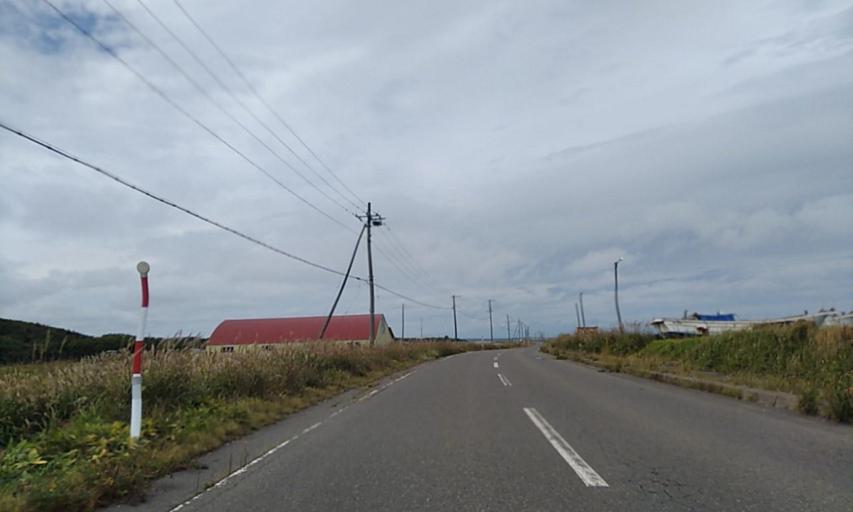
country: JP
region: Hokkaido
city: Shibetsu
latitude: 43.6079
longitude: 145.2799
